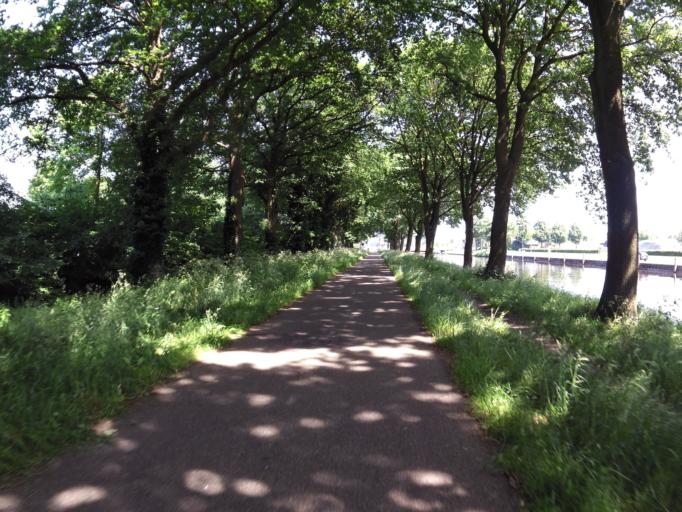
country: NL
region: North Brabant
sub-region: Gemeente Son en Breugel
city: Son
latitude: 51.5051
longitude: 5.4879
